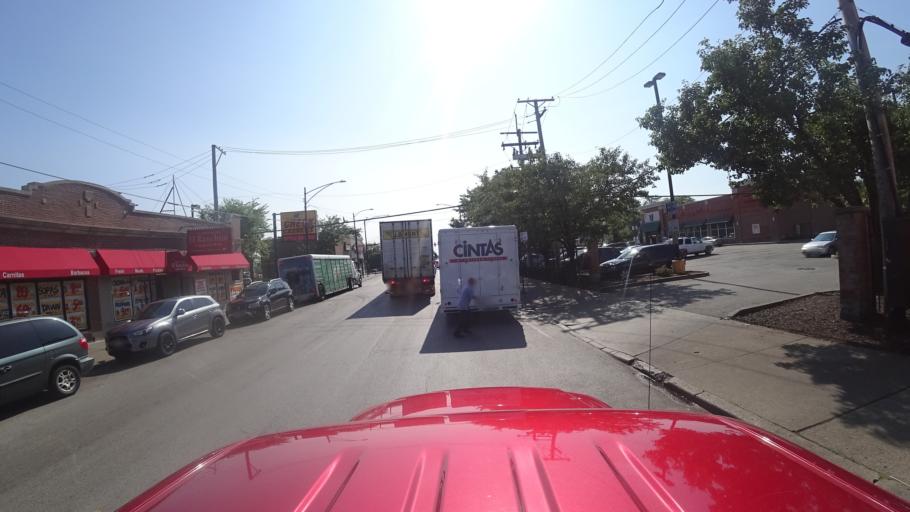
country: US
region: Illinois
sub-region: Cook County
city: Chicago
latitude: 41.8084
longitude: -87.6855
